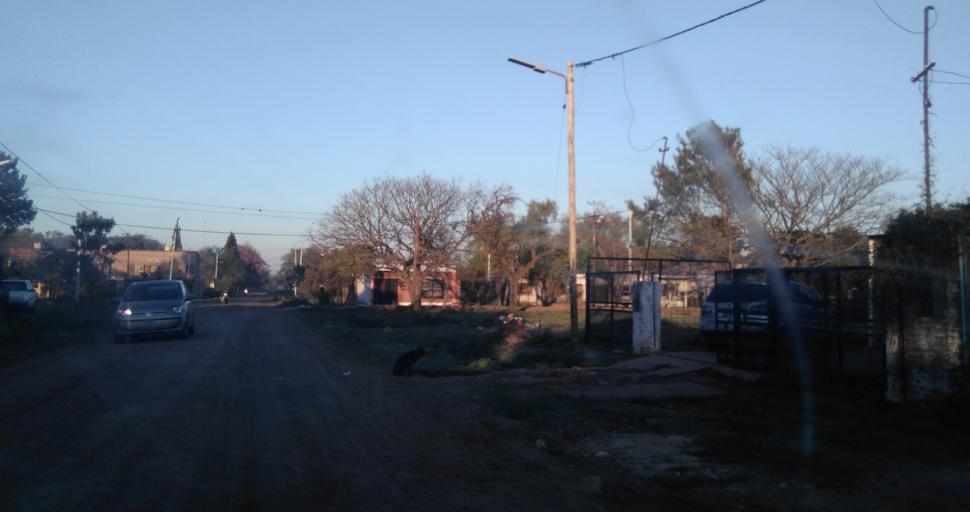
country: AR
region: Chaco
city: Fontana
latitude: -27.4259
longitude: -59.0301
